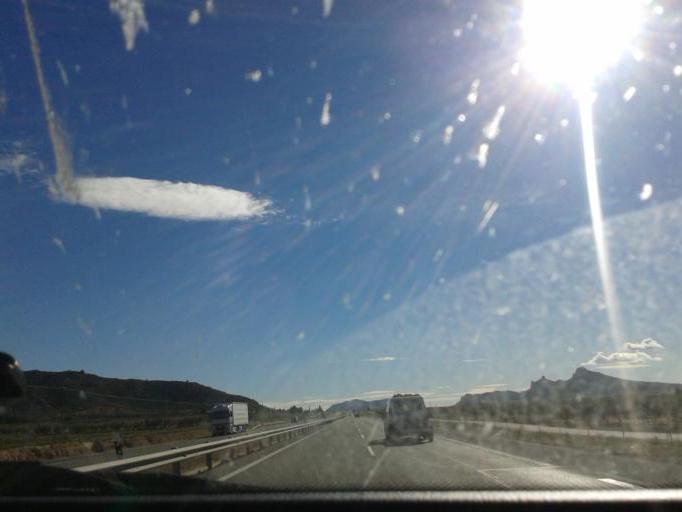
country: ES
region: Valencia
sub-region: Provincia de Alicante
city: Villena
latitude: 38.6021
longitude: -0.8470
